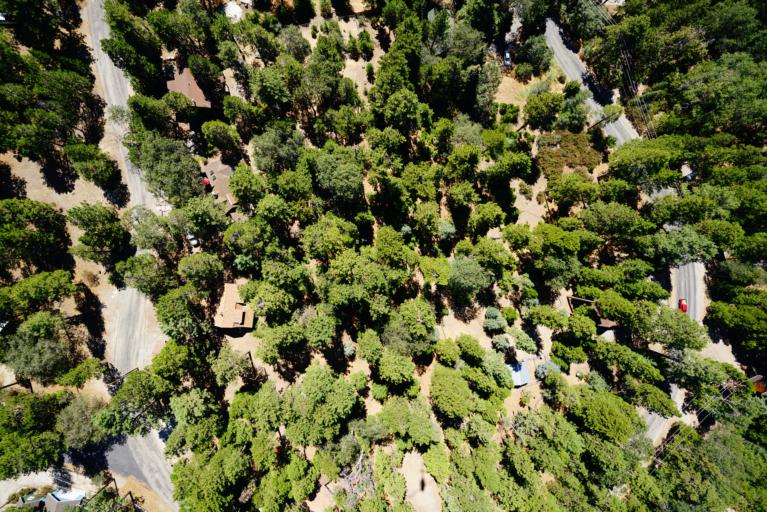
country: US
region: California
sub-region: Riverside County
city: Idyllwild-Pine Cove
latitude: 33.7536
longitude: -116.7427
